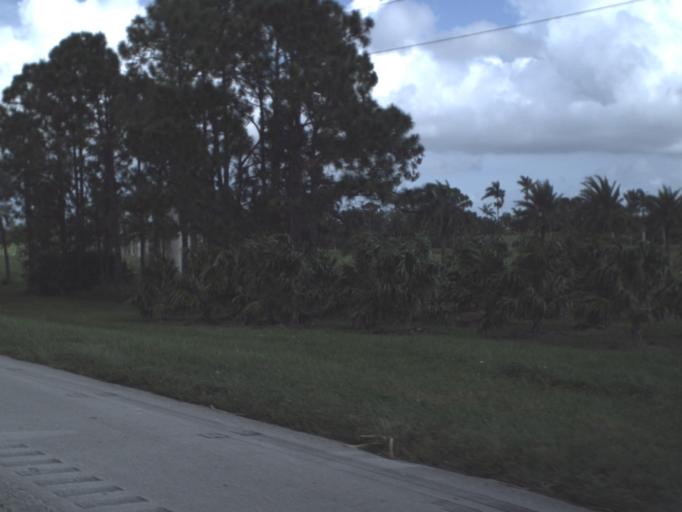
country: US
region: Florida
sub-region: Martin County
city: North River Shores
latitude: 27.2116
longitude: -80.3346
